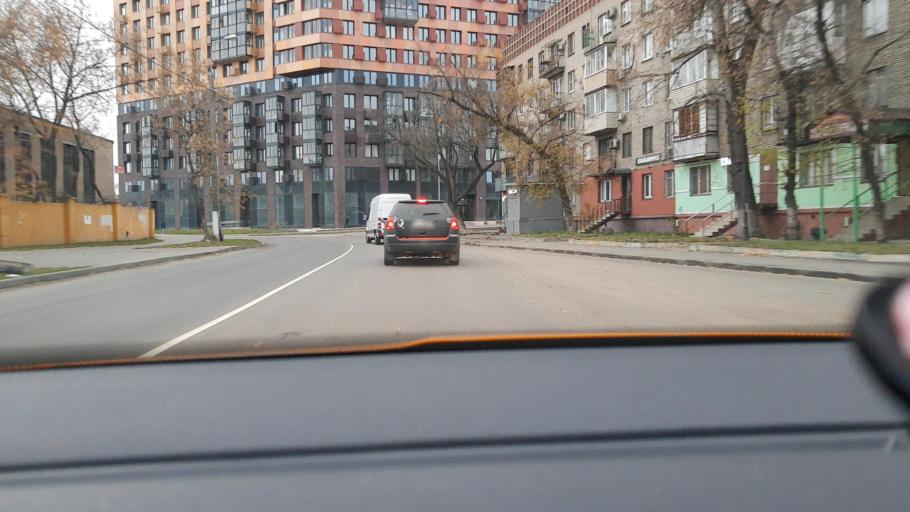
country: RU
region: Moscow
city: Tekstil'shchiki
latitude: 55.7194
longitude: 37.7287
